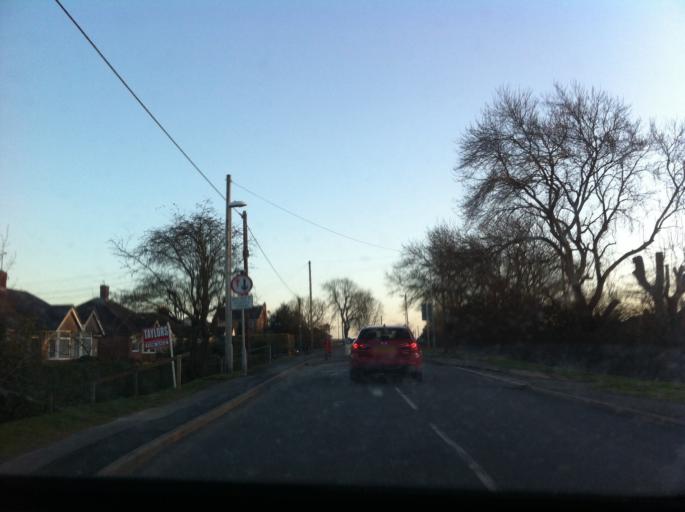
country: GB
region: England
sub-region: Northamptonshire
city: Irchester
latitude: 52.2783
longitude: -0.6543
